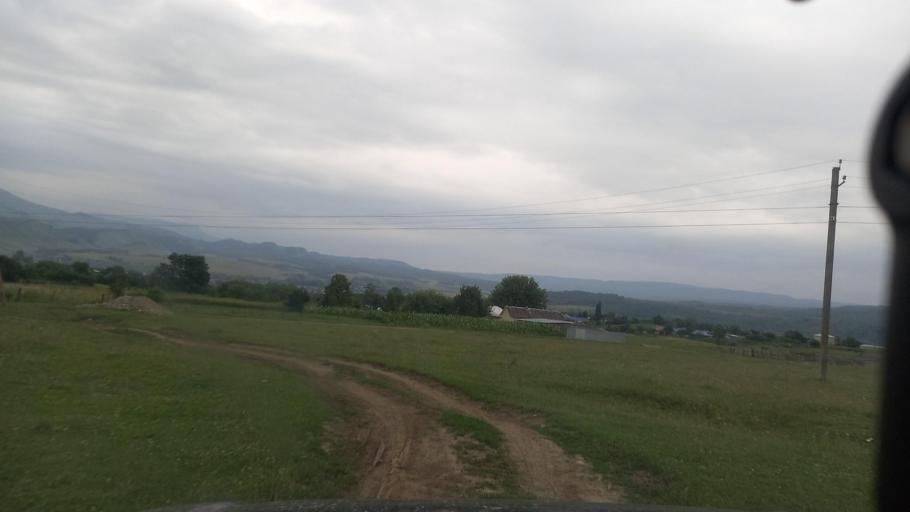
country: RU
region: Karachayevo-Cherkesiya
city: Pregradnaya
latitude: 43.9498
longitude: 41.1708
